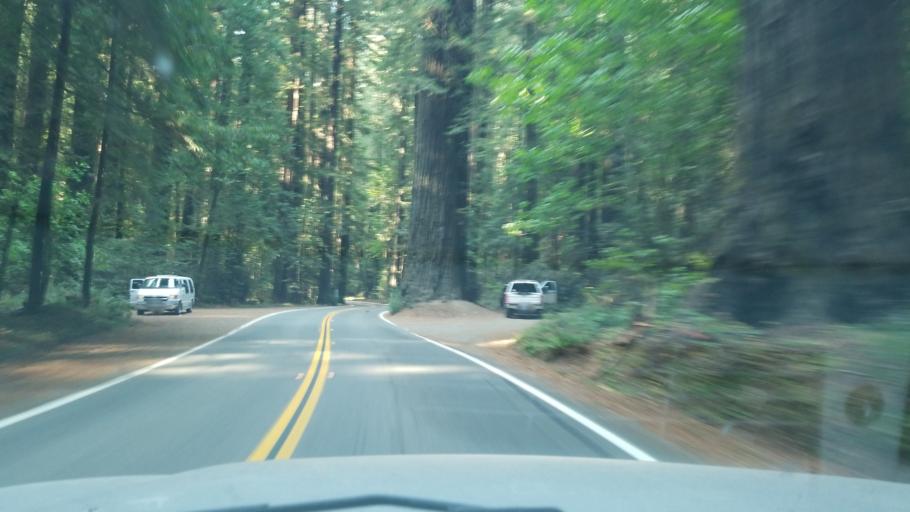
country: US
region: California
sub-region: Humboldt County
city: Redway
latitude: 40.2539
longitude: -123.8207
